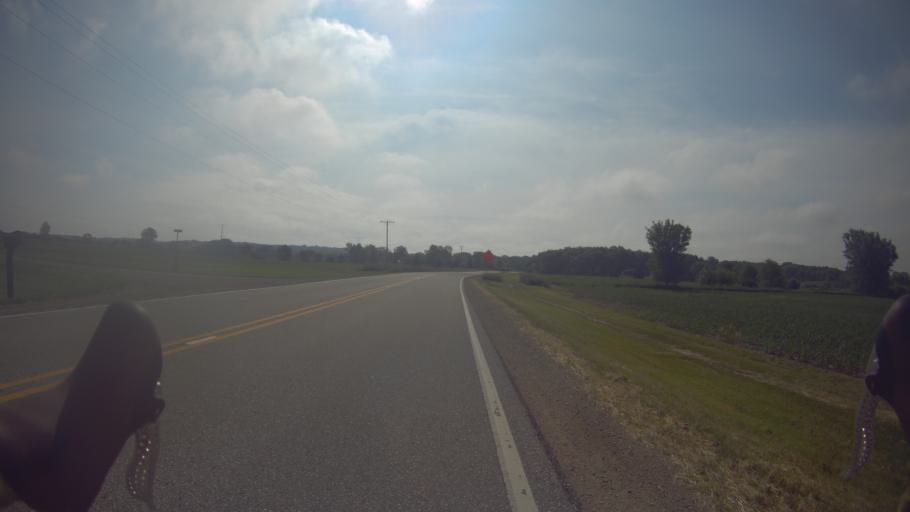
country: US
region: Wisconsin
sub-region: Dane County
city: McFarland
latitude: 43.0150
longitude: -89.2429
